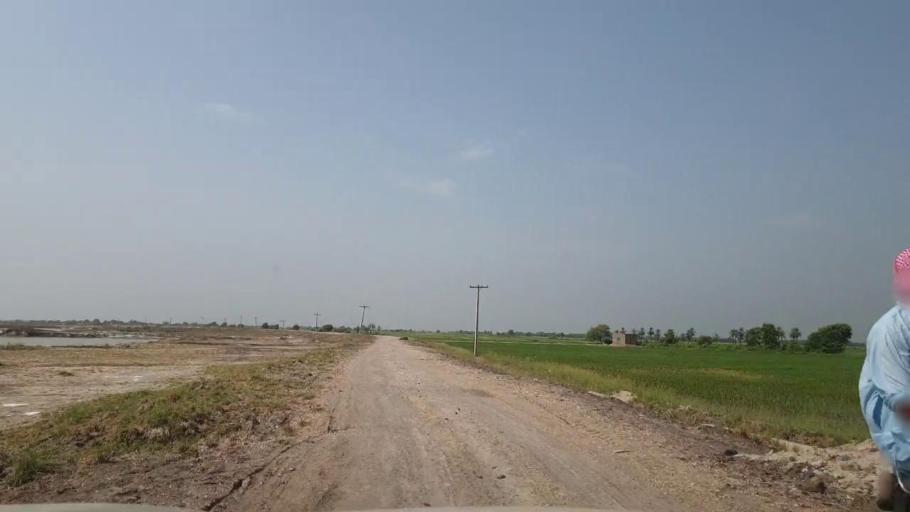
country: PK
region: Sindh
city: Dokri
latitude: 27.4274
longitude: 68.2047
